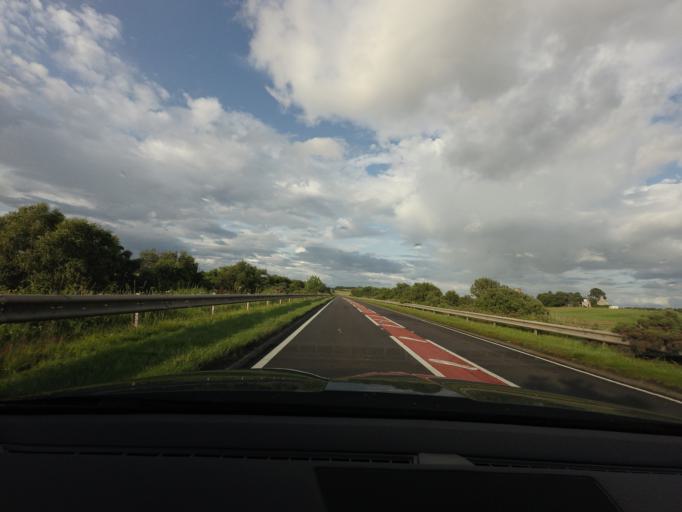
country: GB
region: Scotland
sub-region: Highland
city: Nairn
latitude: 57.5561
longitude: -3.9729
